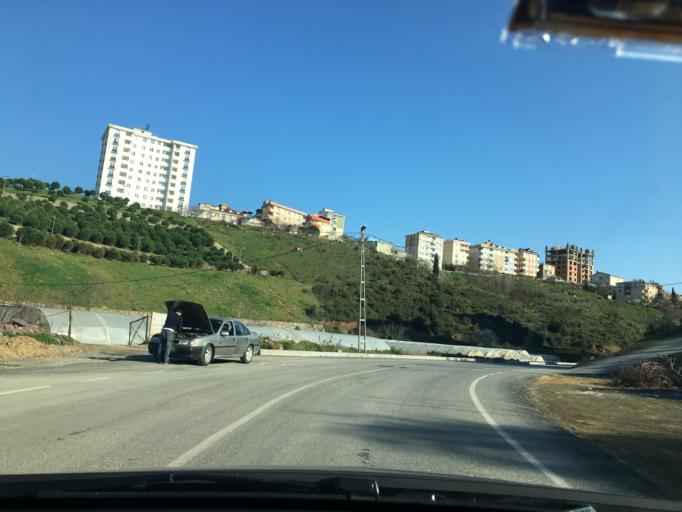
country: TR
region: Istanbul
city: Icmeler
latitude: 40.8727
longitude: 29.3006
